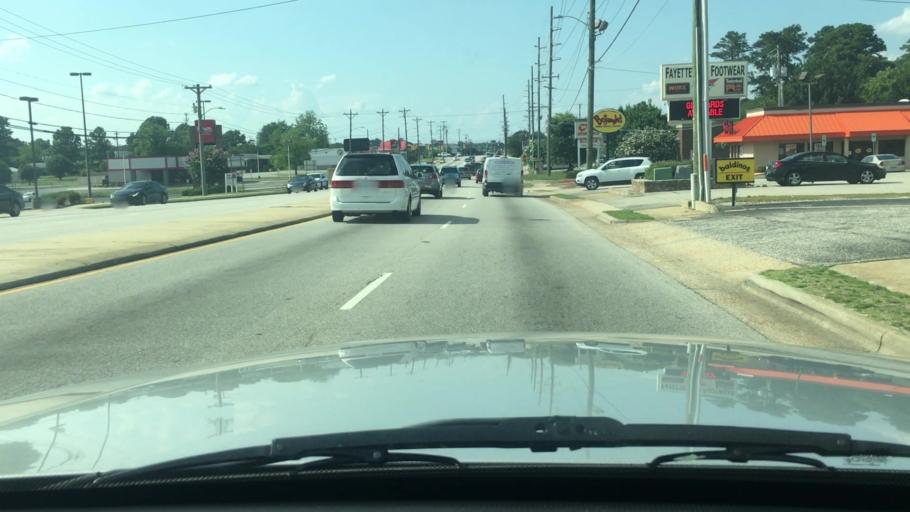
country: US
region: North Carolina
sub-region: Cumberland County
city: Fayetteville
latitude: 35.1058
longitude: -78.8784
